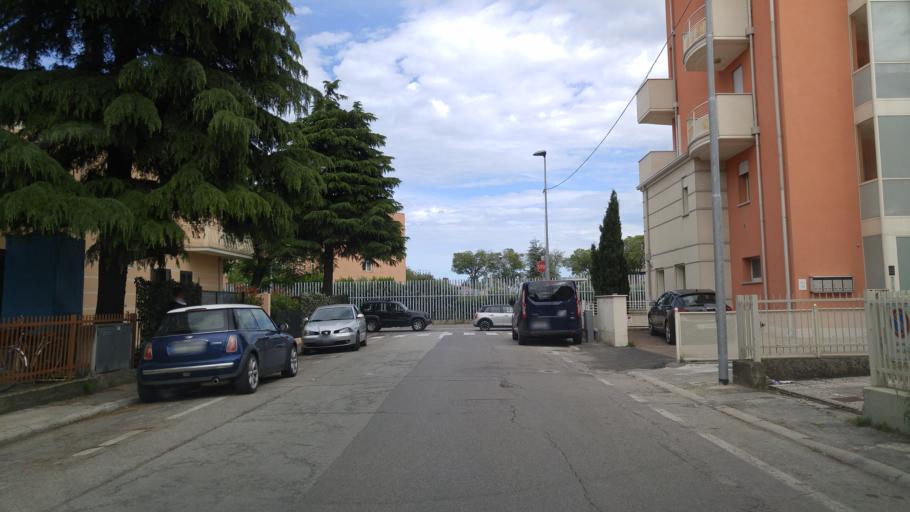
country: IT
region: Emilia-Romagna
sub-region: Provincia di Rimini
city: Rimini
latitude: 44.0459
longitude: 12.5751
